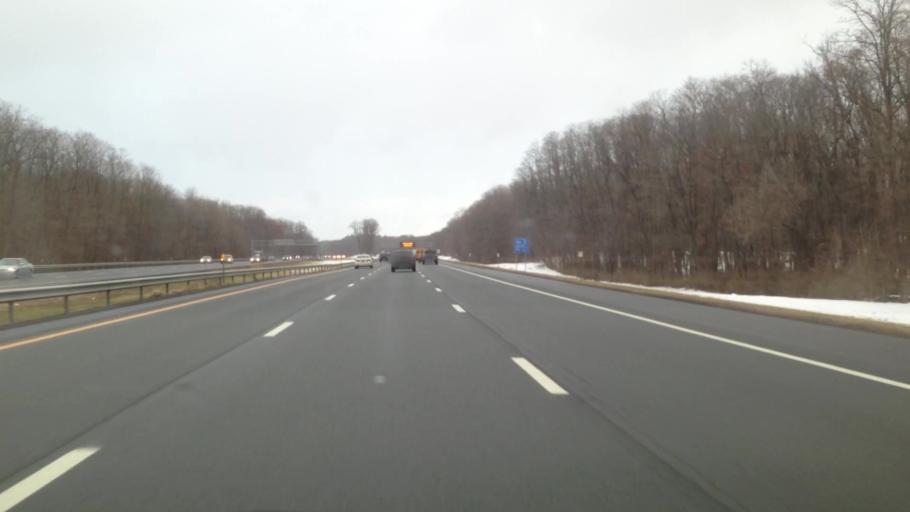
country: US
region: New York
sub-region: Albany County
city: Westmere
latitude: 42.7284
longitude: -73.8927
